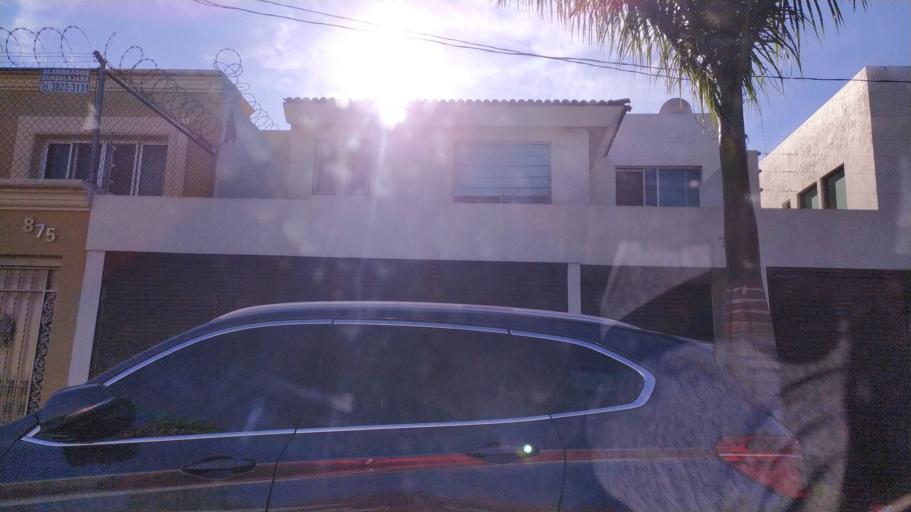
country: MX
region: Jalisco
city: Guadalajara
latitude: 20.6655
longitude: -103.4251
